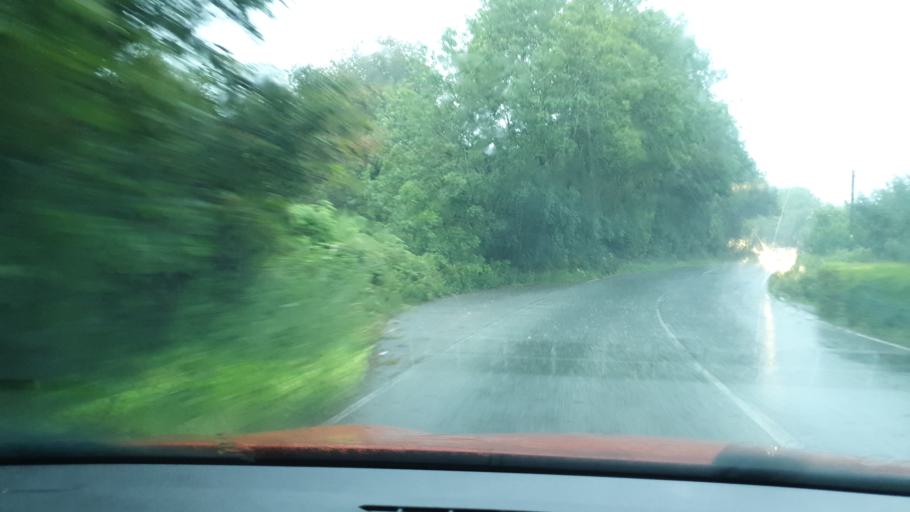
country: GB
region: England
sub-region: Cumbria
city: Askam in Furness
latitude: 54.2600
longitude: -3.2062
